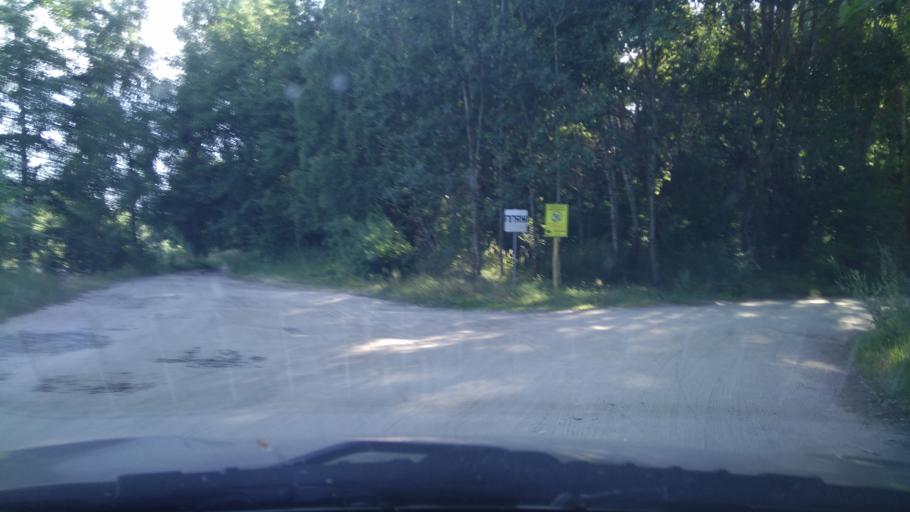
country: BY
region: Brest
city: Byelaazyorsk
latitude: 52.4436
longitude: 25.1740
